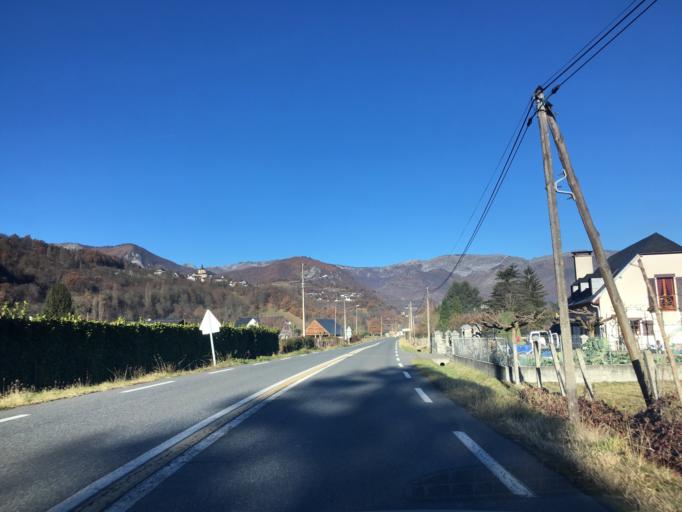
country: FR
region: Midi-Pyrenees
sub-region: Departement des Hautes-Pyrenees
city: Pierrefitte-Nestalas
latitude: 42.9756
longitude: -0.0794
